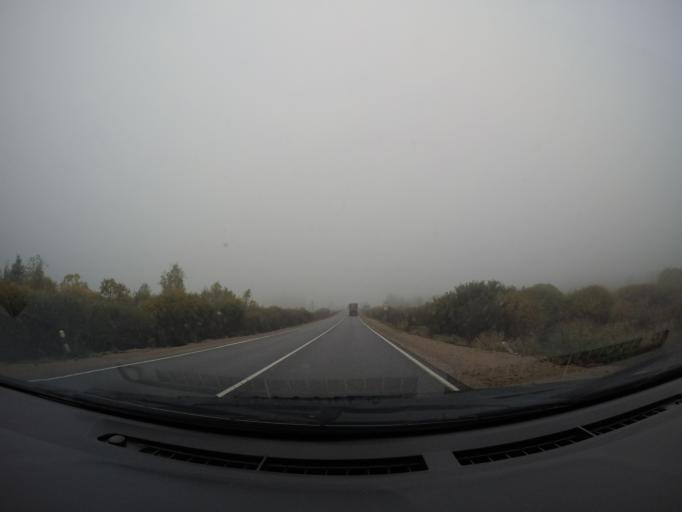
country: RU
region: Moskovskaya
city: Novopetrovskoye
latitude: 55.8367
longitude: 36.4533
